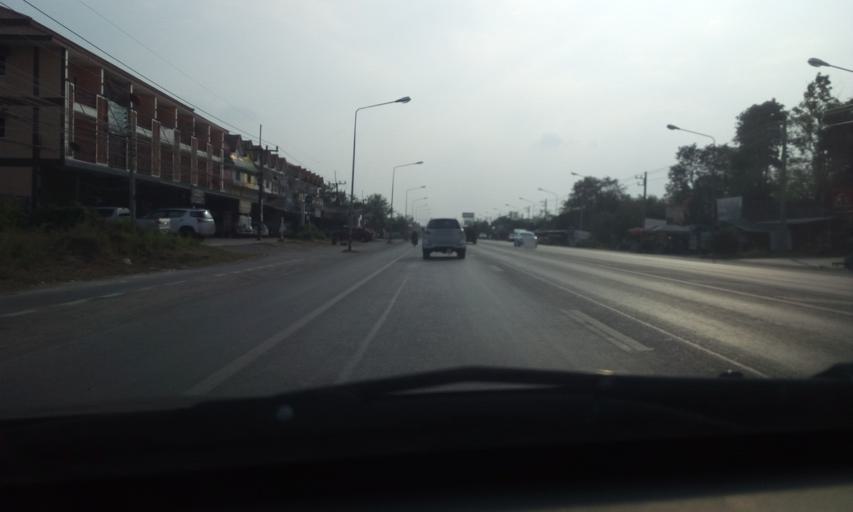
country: TH
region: Nakhon Nayok
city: Nakhon Nayok
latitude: 14.2318
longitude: 101.2397
